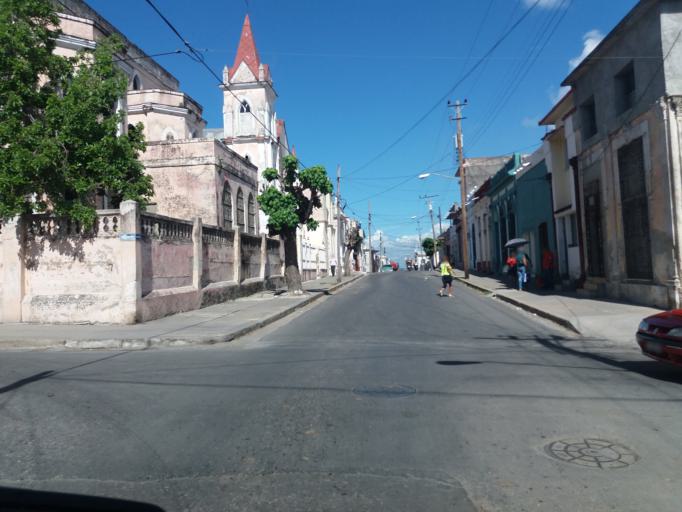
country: CU
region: Cienfuegos
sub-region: Municipio de Cienfuegos
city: Cienfuegos
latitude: 22.1474
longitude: -80.4460
